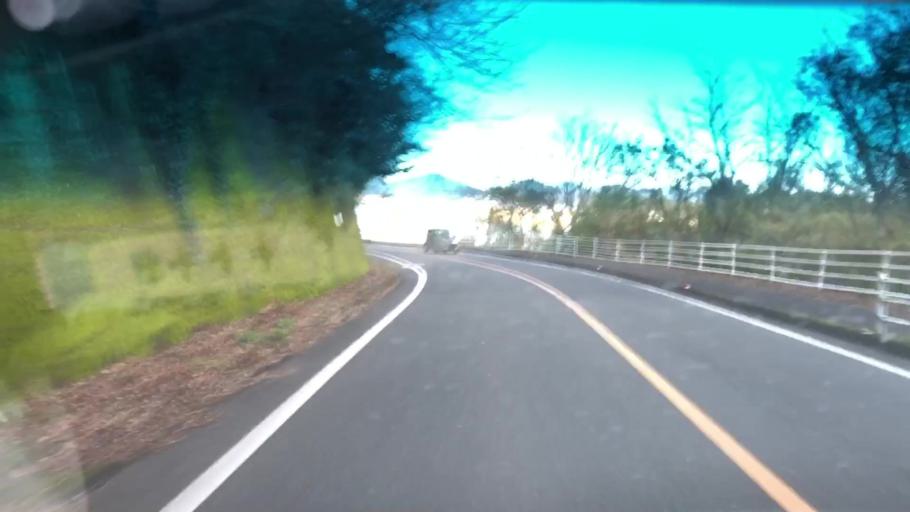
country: JP
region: Kagoshima
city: Satsumasendai
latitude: 31.8164
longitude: 130.2892
